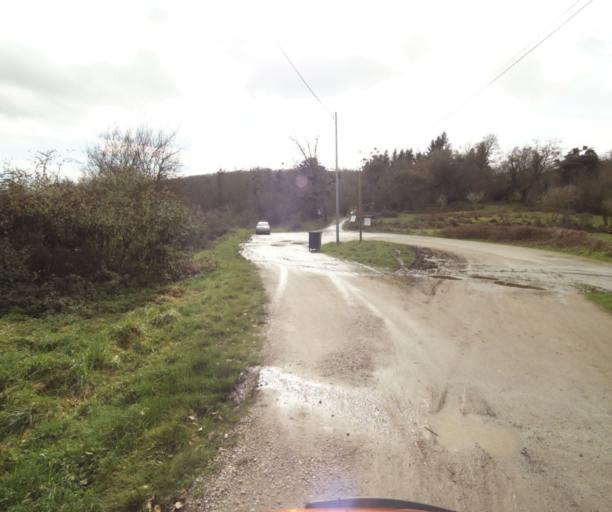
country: FR
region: Midi-Pyrenees
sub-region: Departement de l'Ariege
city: Pamiers
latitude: 43.1099
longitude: 1.6013
